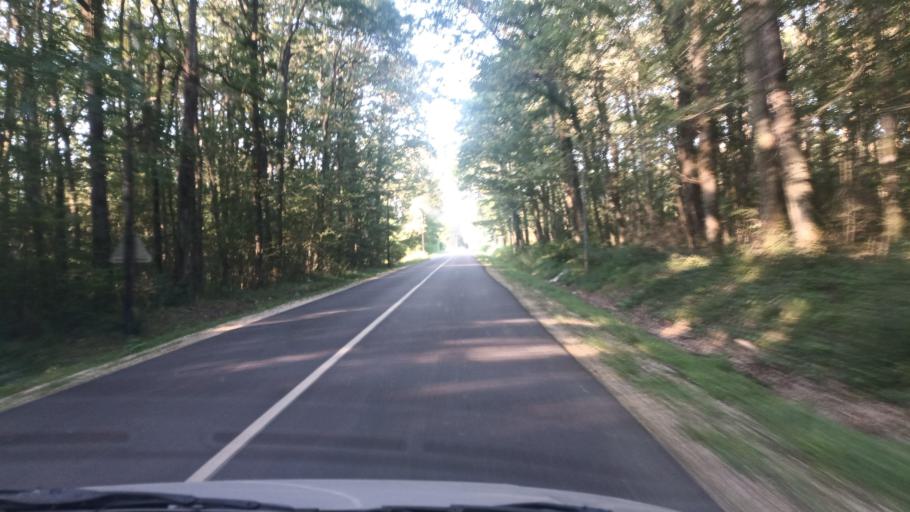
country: FR
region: Bourgogne
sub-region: Departement de l'Yonne
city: Pont-sur-Yonne
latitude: 48.2588
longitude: 3.1723
